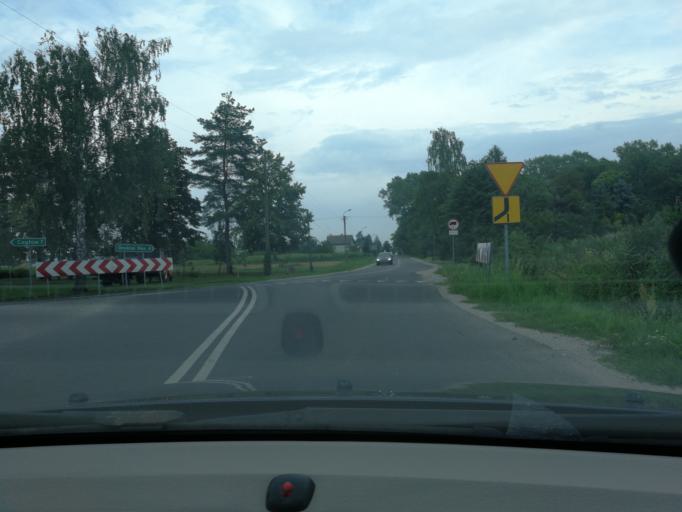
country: PL
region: Masovian Voivodeship
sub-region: Powiat warszawski zachodni
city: Bieniewice
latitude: 52.1197
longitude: 20.5671
